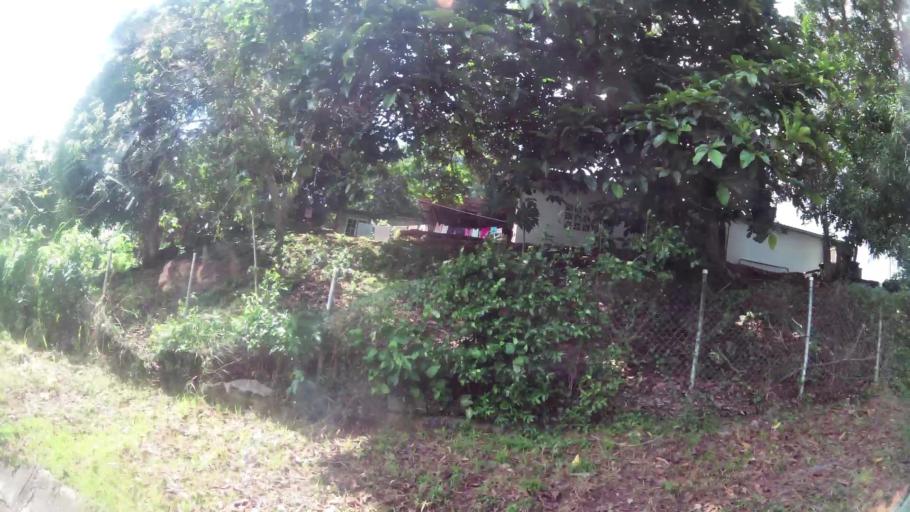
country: PA
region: Panama
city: Vista Alegre
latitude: 8.9248
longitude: -79.7045
